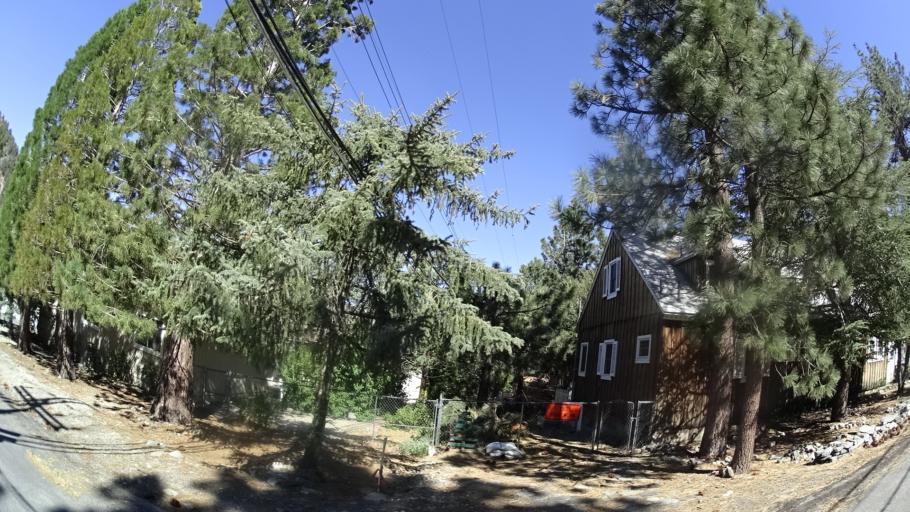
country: US
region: California
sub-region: San Bernardino County
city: Wrightwood
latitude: 34.3639
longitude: -117.6466
